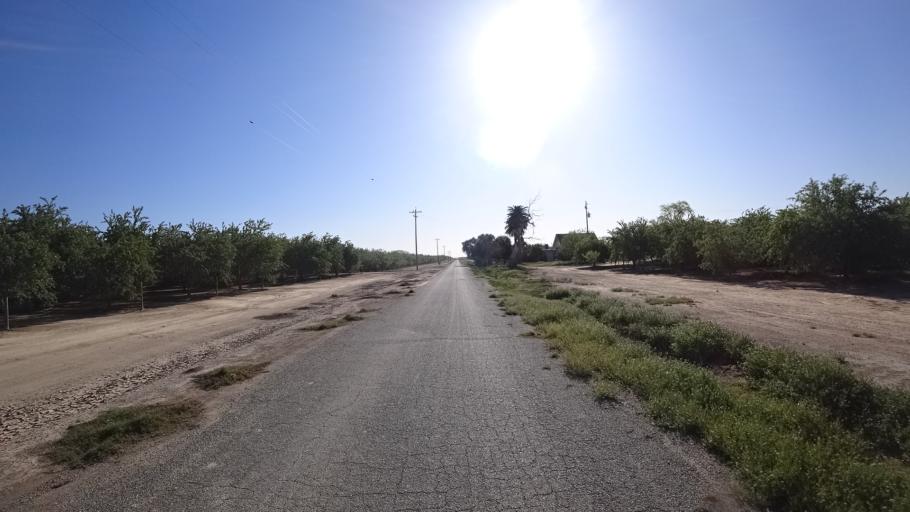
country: US
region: California
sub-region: Glenn County
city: Hamilton City
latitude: 39.6948
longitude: -122.0603
